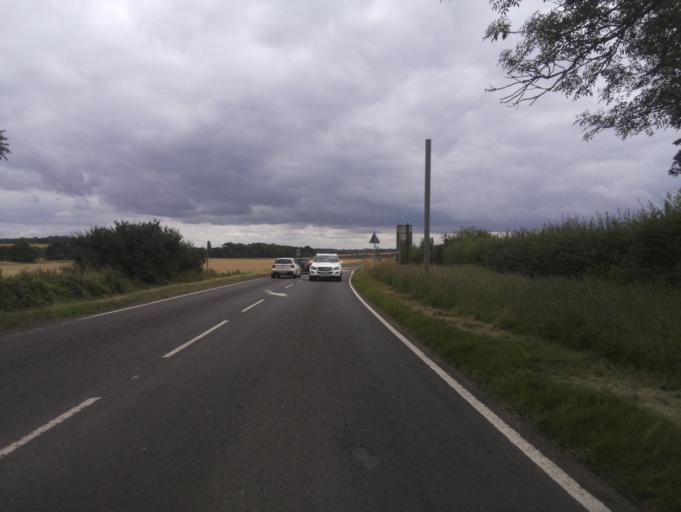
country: GB
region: England
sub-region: District of Rutland
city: Ryhall
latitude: 52.6778
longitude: -0.4713
